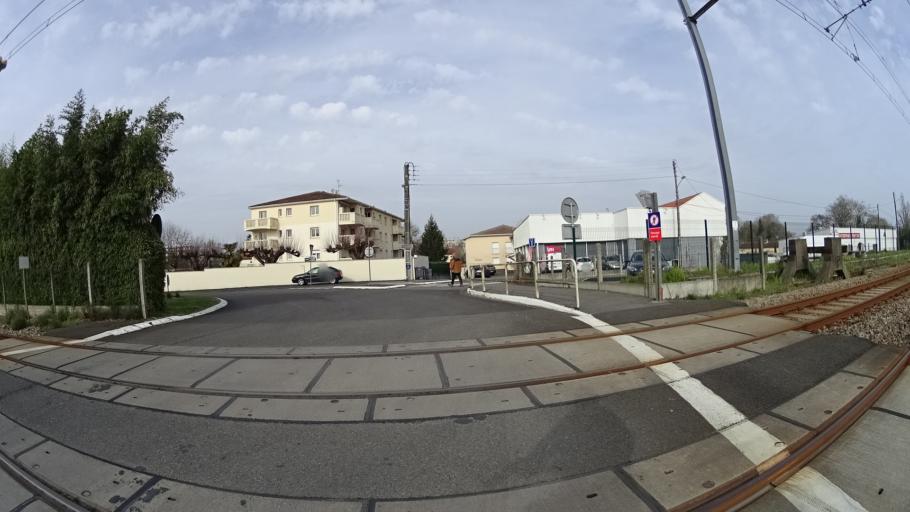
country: FR
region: Aquitaine
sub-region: Departement des Landes
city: Dax
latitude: 43.6988
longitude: -1.0541
